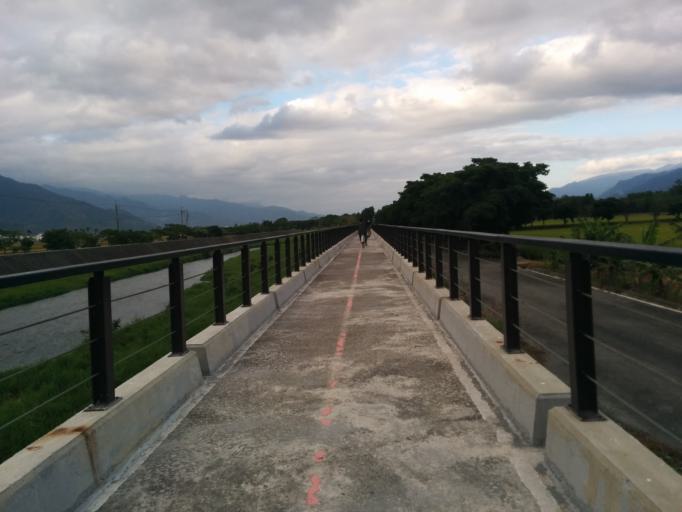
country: TW
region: Taiwan
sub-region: Taitung
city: Taitung
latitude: 23.0328
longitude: 121.1690
